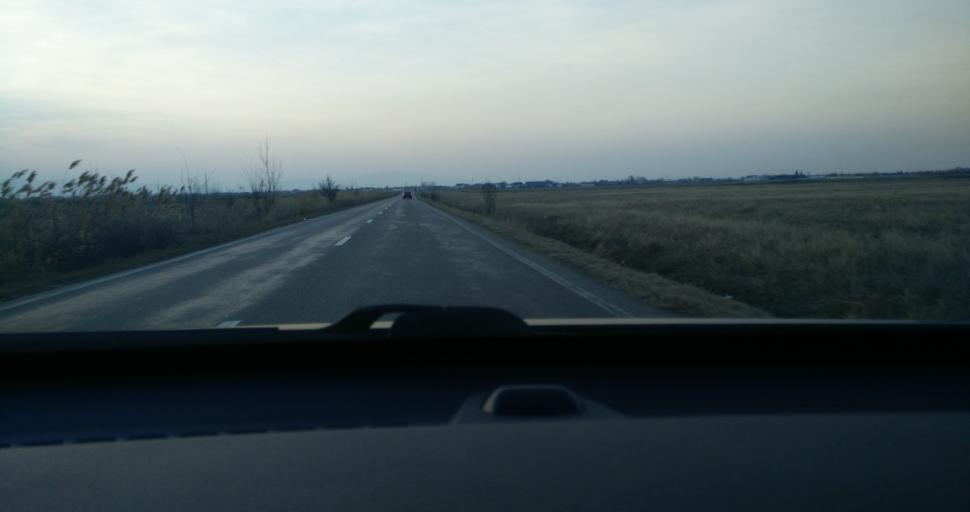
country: RO
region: Vrancea
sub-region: Comuna Milcovul
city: Milcovul
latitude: 45.6717
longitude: 27.2586
